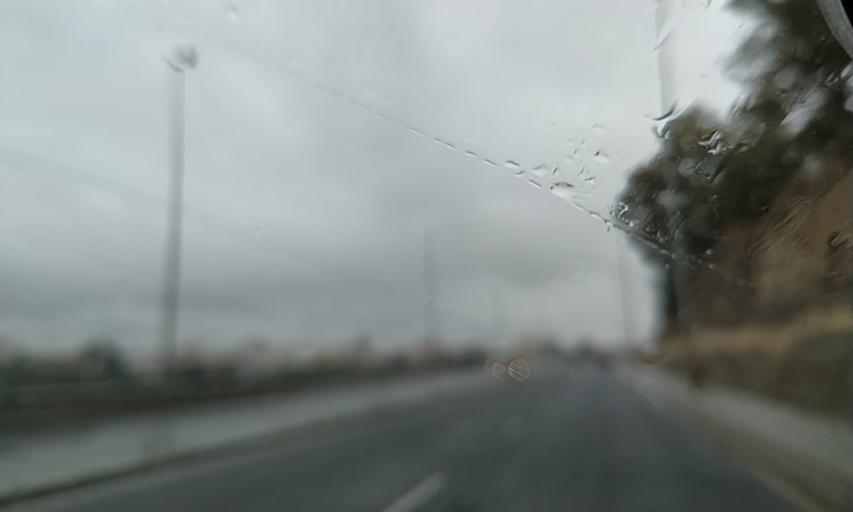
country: ES
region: Extremadura
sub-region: Provincia de Badajoz
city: Badajoz
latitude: 38.8880
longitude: -6.9718
